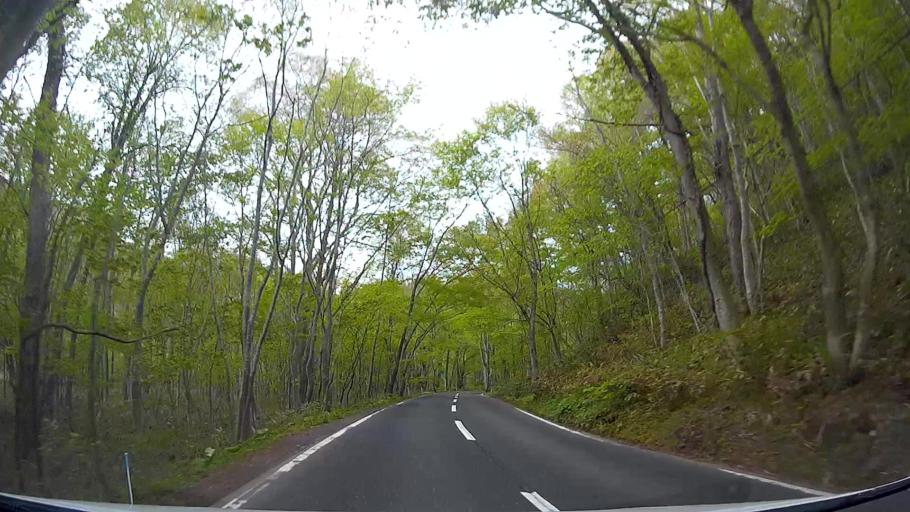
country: JP
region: Aomori
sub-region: Aomori Shi
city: Furudate
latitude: 40.5718
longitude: 140.9785
